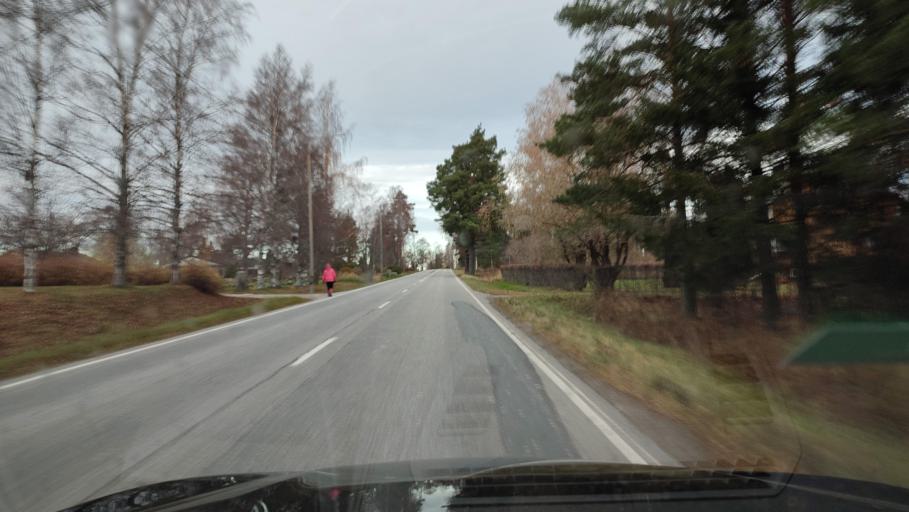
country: FI
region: Ostrobothnia
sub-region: Sydosterbotten
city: Naerpes
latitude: 62.4200
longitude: 21.3425
